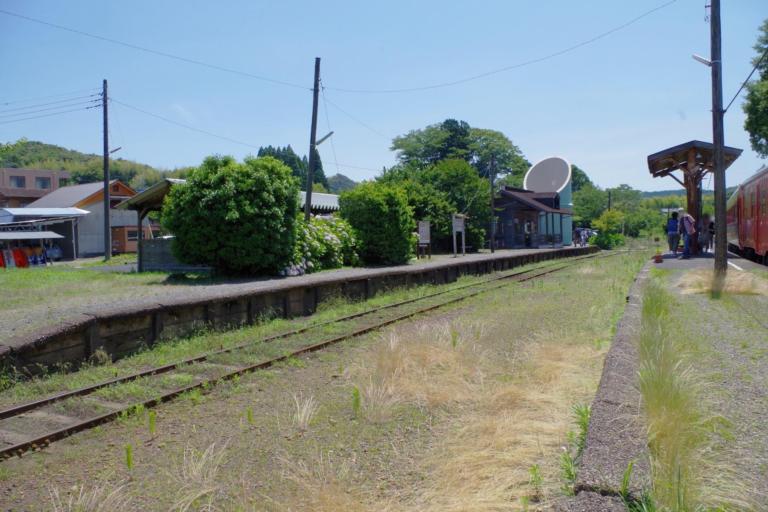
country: JP
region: Chiba
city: Katsuura
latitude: 35.2501
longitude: 140.1994
